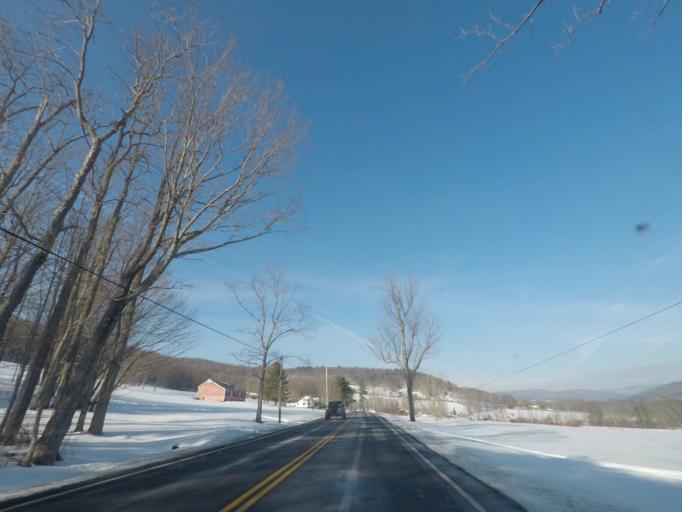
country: US
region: Massachusetts
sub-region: Berkshire County
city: Richmond
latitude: 42.4931
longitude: -73.3869
